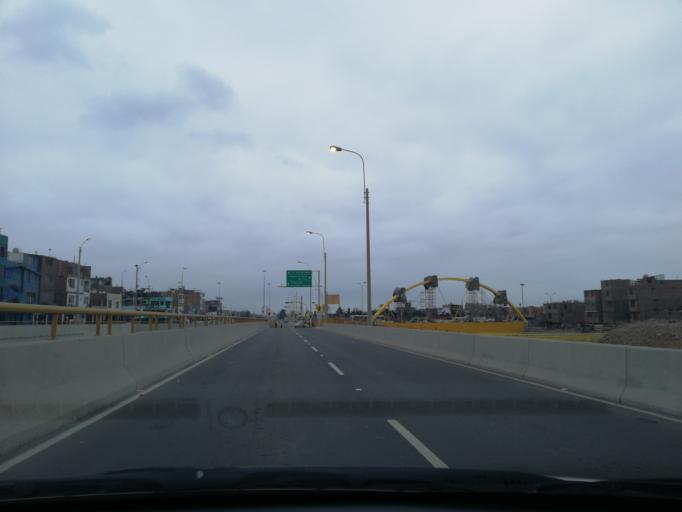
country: PE
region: Callao
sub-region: Callao
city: Callao
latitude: -12.0355
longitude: -77.0764
